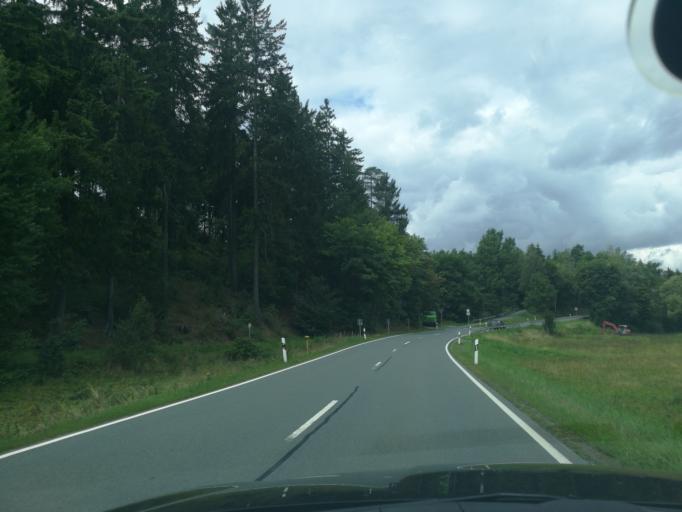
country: DE
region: Saxony
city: Adorf
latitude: 50.3453
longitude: 12.2379
